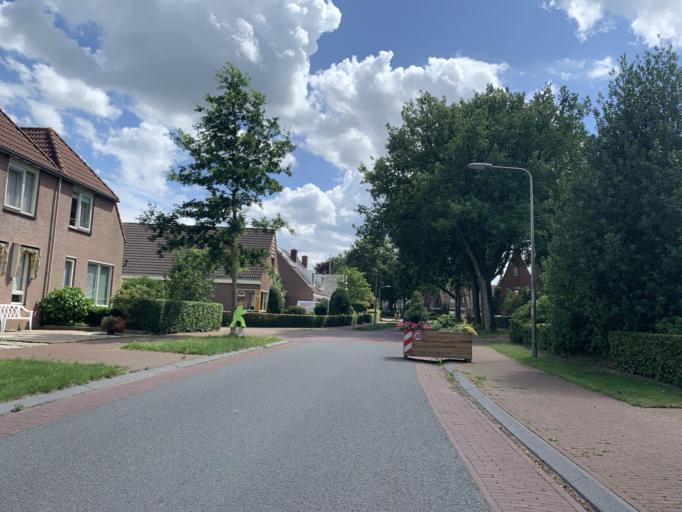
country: NL
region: Groningen
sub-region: Gemeente Haren
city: Haren
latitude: 53.1570
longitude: 6.6417
